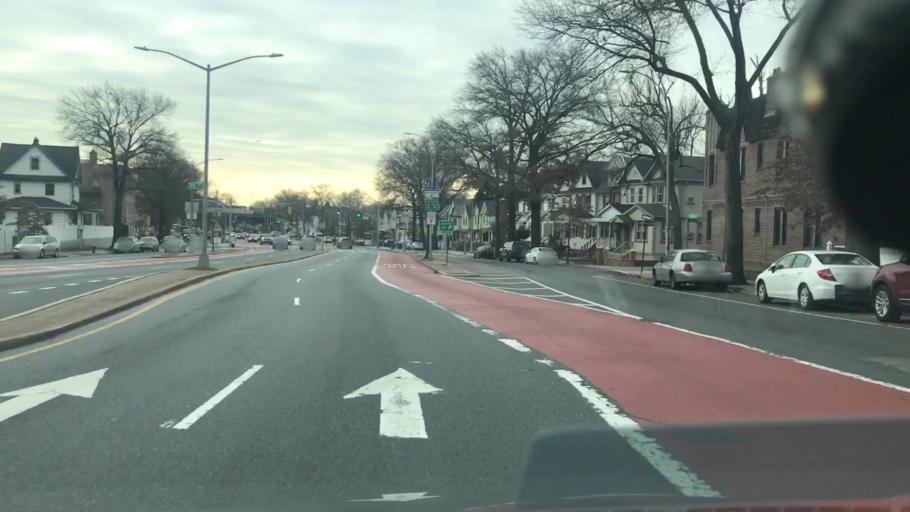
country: US
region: New York
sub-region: Queens County
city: Borough of Queens
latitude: 40.6973
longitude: -73.8529
